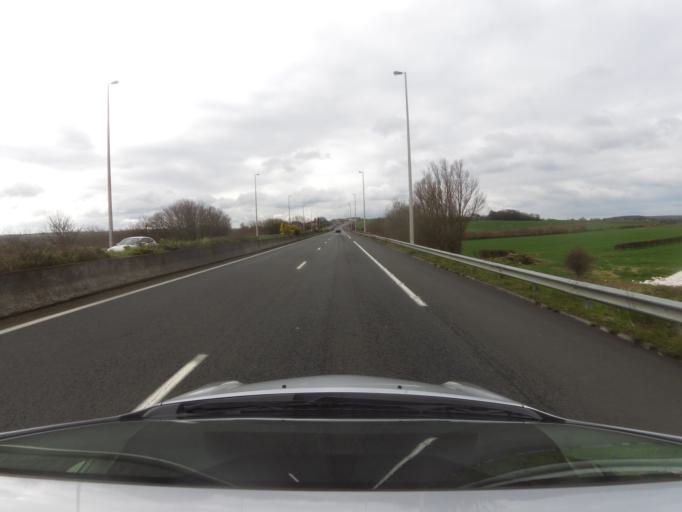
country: FR
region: Nord-Pas-de-Calais
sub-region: Departement du Pas-de-Calais
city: Marquise
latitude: 50.8014
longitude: 1.6904
